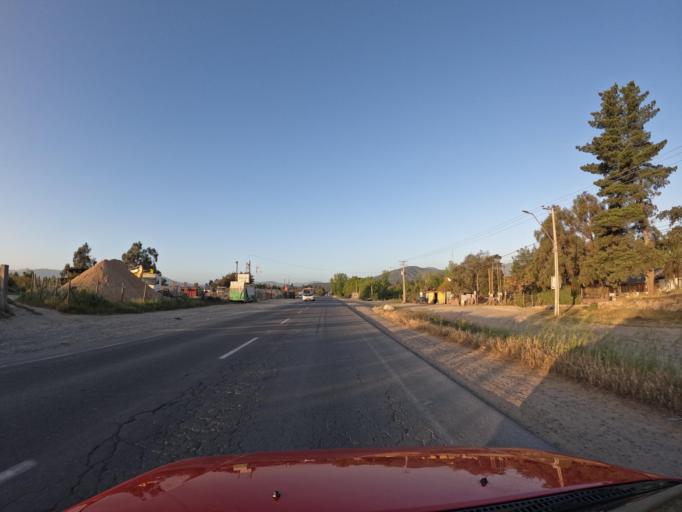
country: CL
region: O'Higgins
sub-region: Provincia de Cachapoal
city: San Vicente
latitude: -34.1569
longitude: -71.3888
